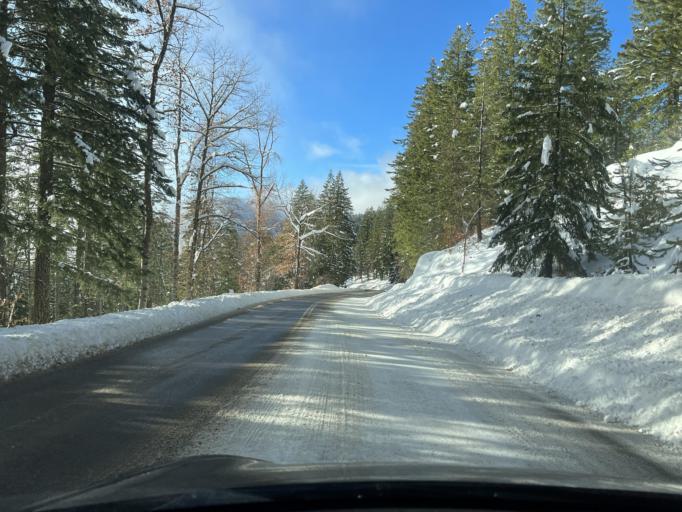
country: US
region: Idaho
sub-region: Bonner County
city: Ponderay
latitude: 48.3394
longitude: -116.6050
